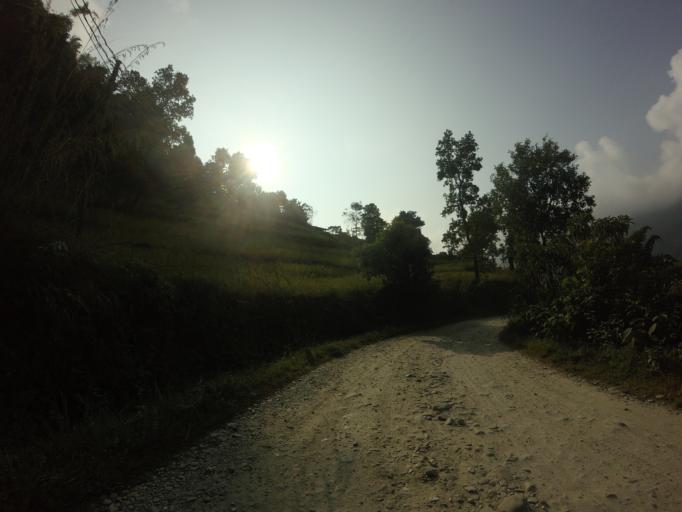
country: NP
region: Western Region
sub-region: Gandaki Zone
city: Pokhara
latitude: 28.2338
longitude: 83.9171
